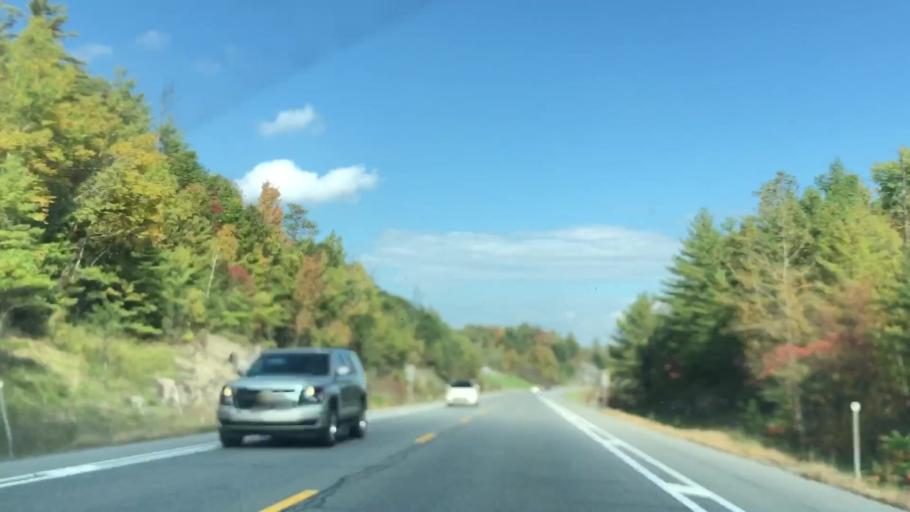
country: US
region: New York
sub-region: Washington County
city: Whitehall
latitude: 43.4666
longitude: -73.4397
